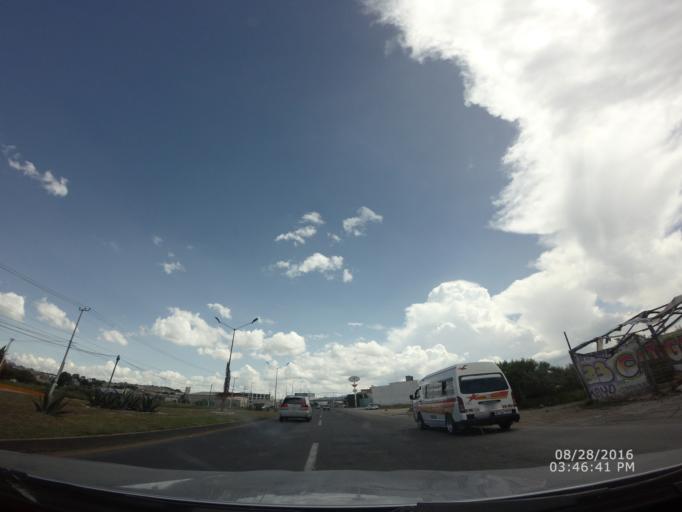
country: MX
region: Hidalgo
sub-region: Mineral de la Reforma
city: Nuevo Centro de Poblacion Agricola el Chacon
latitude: 20.0733
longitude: -98.7449
